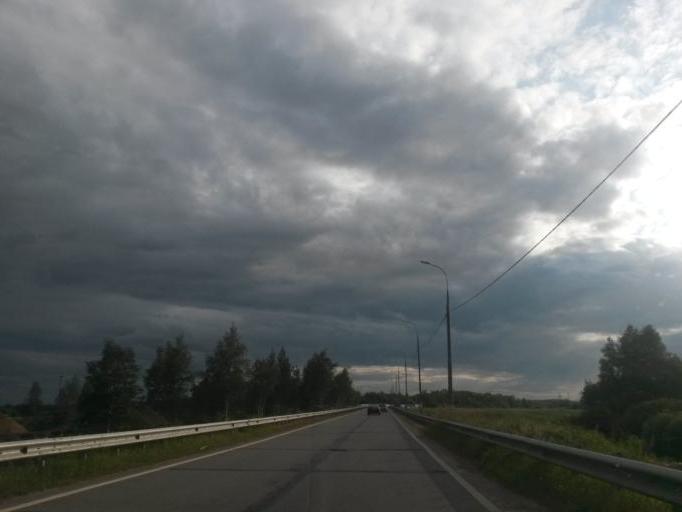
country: RU
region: Moskovskaya
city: L'vovskiy
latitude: 55.3340
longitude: 37.5642
